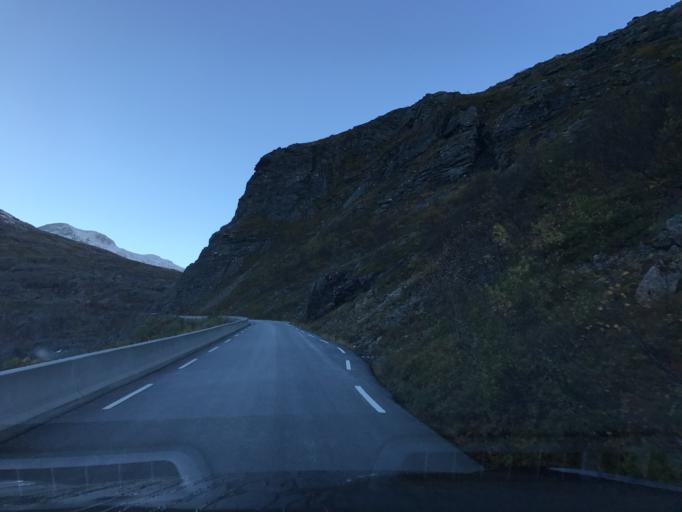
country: NO
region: More og Romsdal
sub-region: Rauma
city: Andalsnes
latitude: 62.4598
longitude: 7.6663
